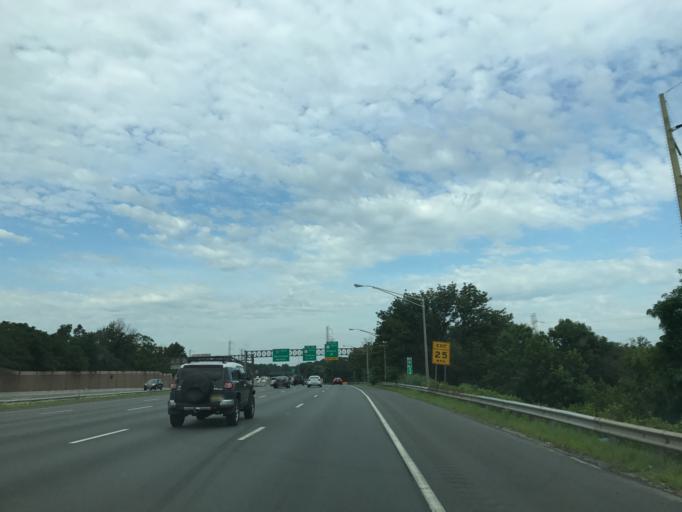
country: US
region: New Jersey
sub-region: Middlesex County
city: Metuchen
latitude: 40.5297
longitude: -74.3472
